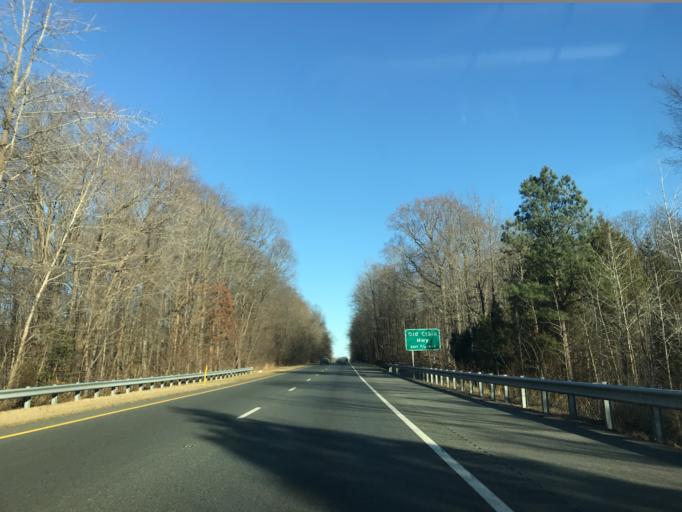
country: US
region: Maryland
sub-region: Prince George's County
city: Upper Marlboro
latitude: 38.8114
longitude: -76.7850
